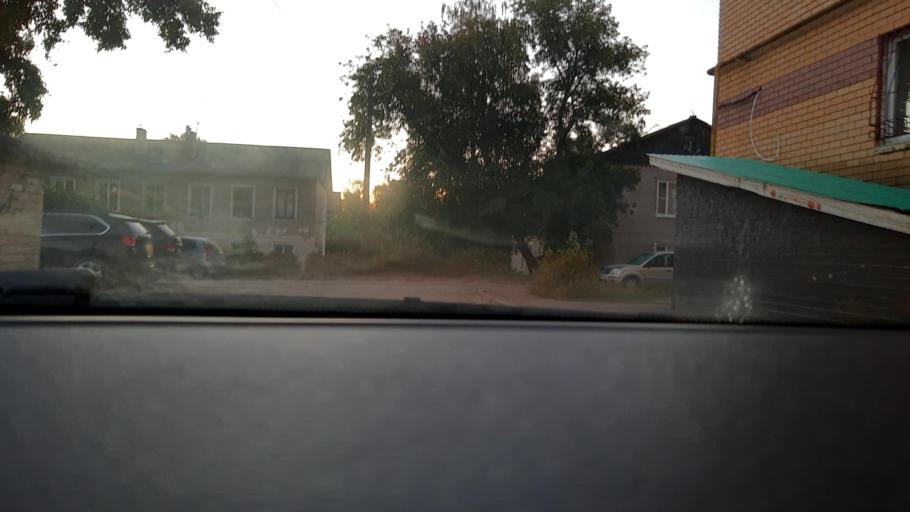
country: RU
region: Nizjnij Novgorod
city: Bor
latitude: 56.3377
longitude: 44.1091
